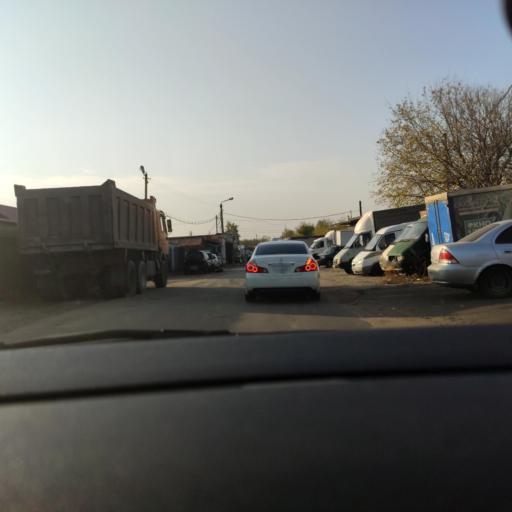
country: RU
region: Voronezj
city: Podgornoye
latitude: 51.7004
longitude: 39.1293
